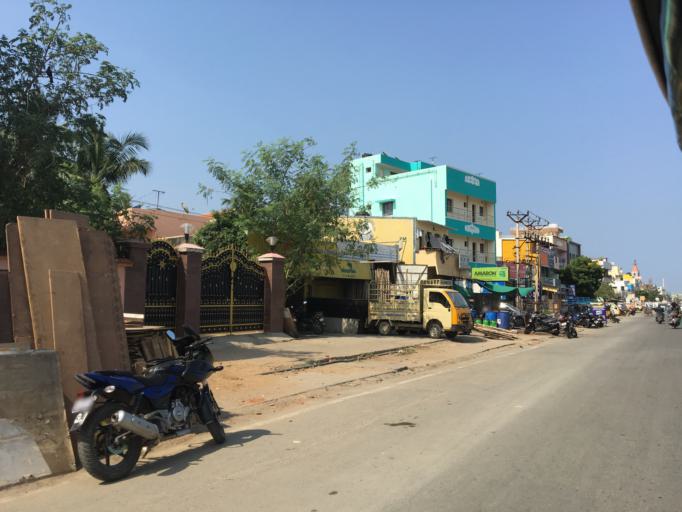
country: IN
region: Tamil Nadu
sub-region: Kancheepuram
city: Perungudi
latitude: 12.9812
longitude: 80.2355
